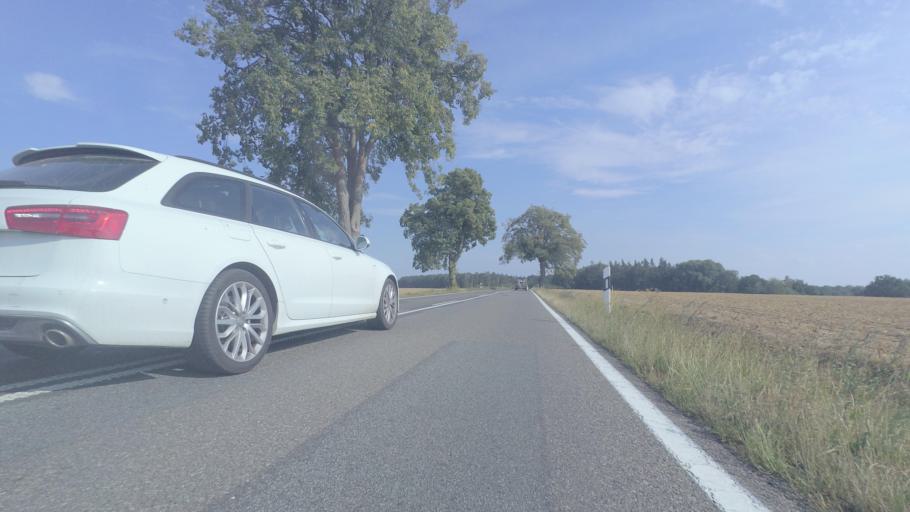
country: DE
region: Mecklenburg-Vorpommern
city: Grimmen
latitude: 54.0804
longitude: 13.1049
